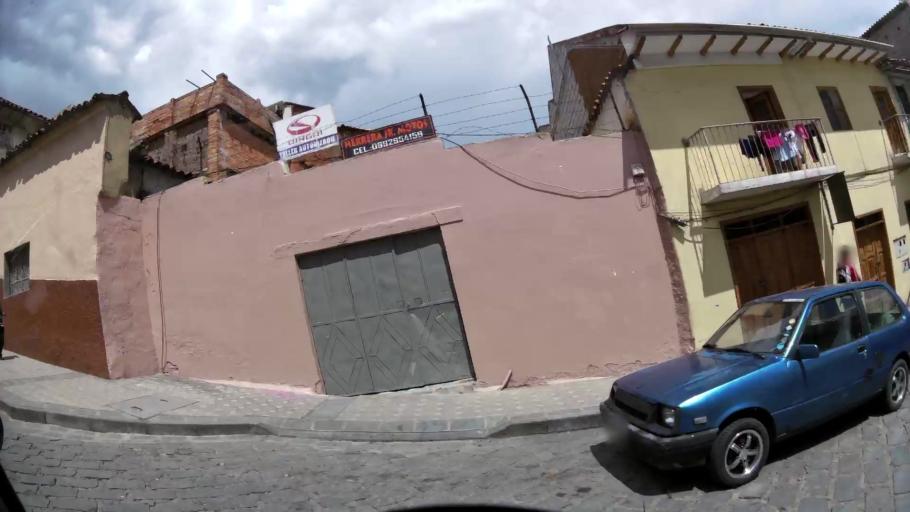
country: EC
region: Azuay
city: Cuenca
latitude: -2.8921
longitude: -78.9990
